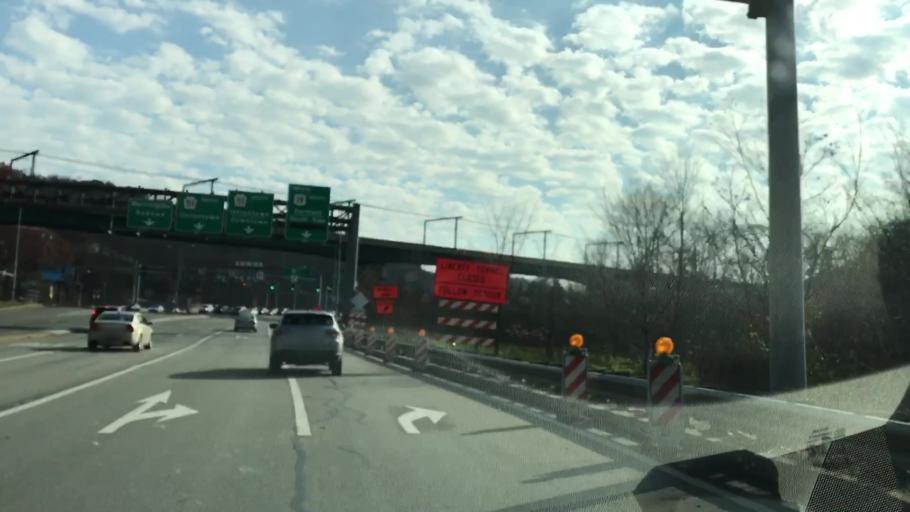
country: US
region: Pennsylvania
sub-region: Allegheny County
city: Mount Oliver
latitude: 40.4154
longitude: -80.0131
